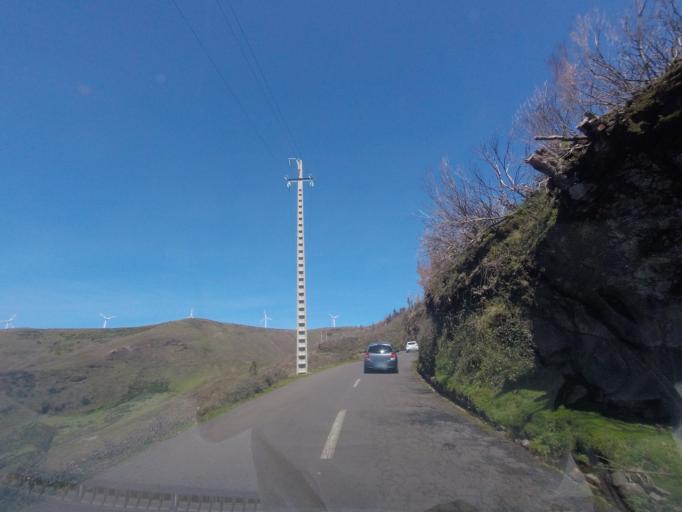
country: PT
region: Madeira
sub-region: Calheta
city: Arco da Calheta
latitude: 32.7364
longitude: -17.1039
